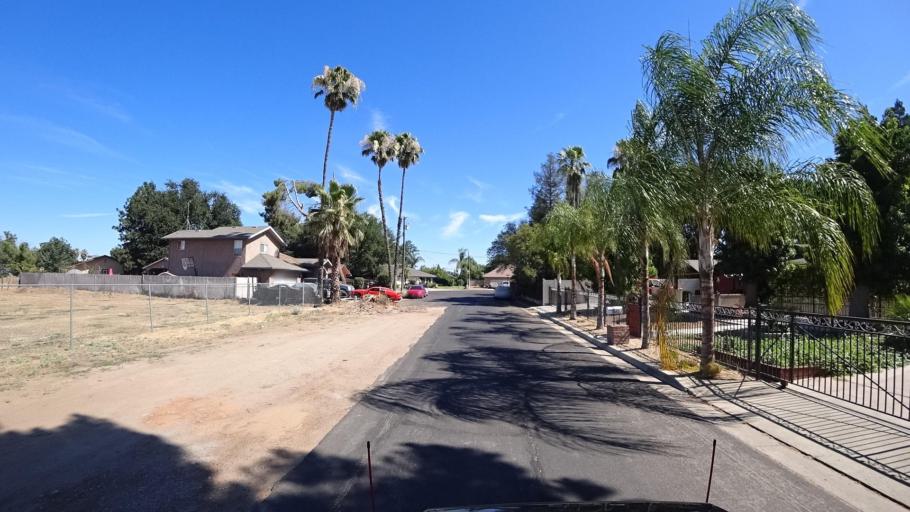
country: US
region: California
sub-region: Fresno County
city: Sunnyside
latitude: 36.7417
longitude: -119.7161
